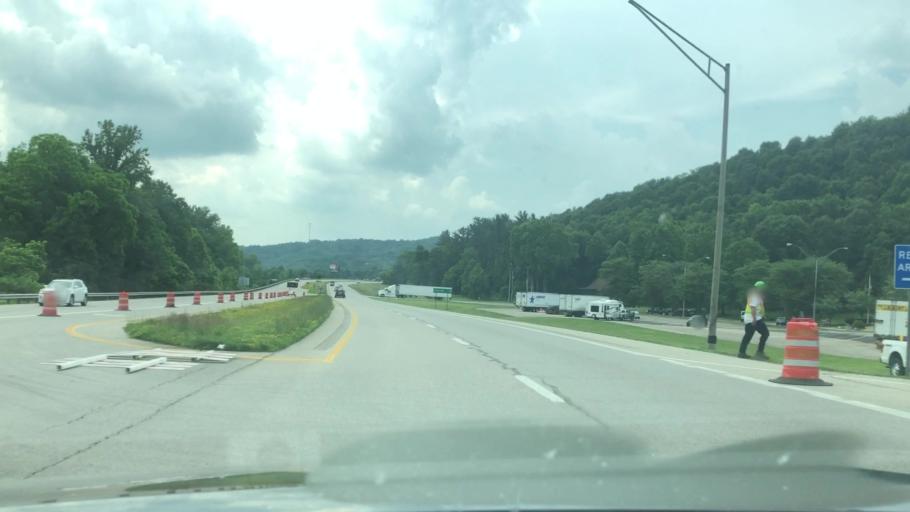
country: US
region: Ohio
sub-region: Jackson County
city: Jackson
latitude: 39.1644
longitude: -82.7363
